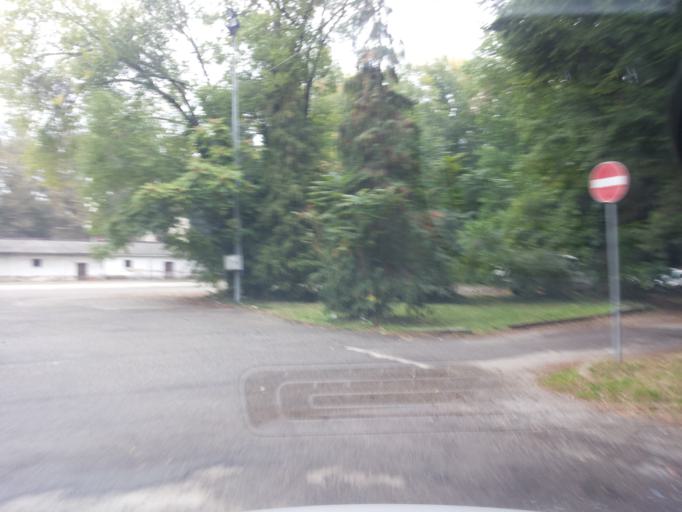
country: IT
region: Piedmont
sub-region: Provincia di Vercelli
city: Vercelli
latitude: 45.3256
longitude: 8.4293
